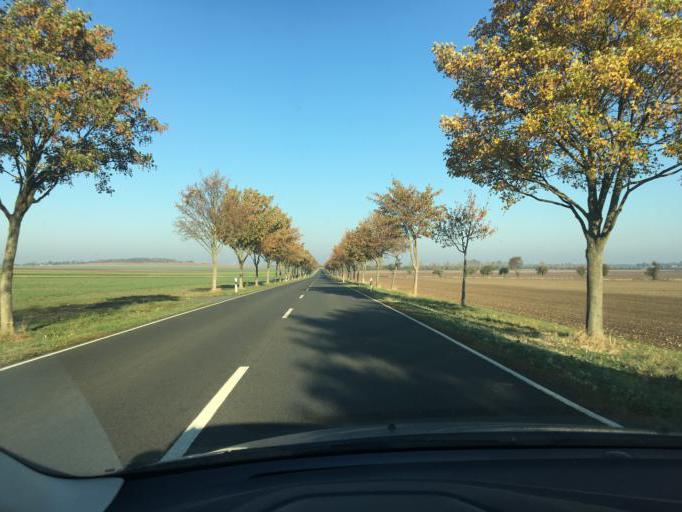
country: DE
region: Saxony-Anhalt
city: Wanzleben
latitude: 52.0205
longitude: 11.4977
